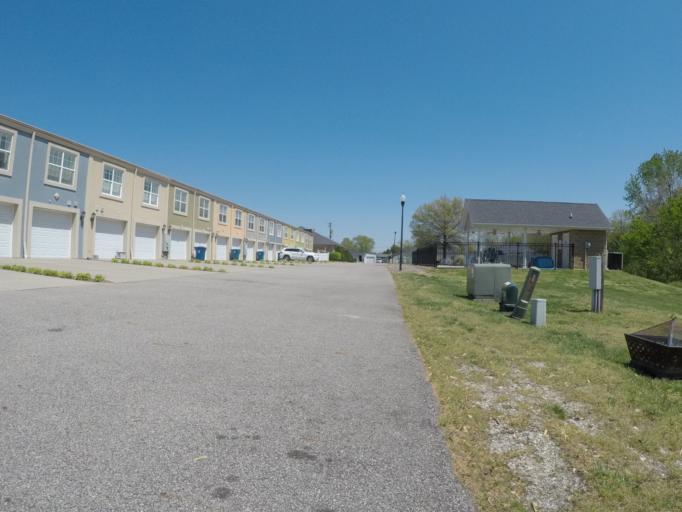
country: US
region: West Virginia
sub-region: Cabell County
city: Pea Ridge
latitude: 38.4119
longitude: -82.3084
